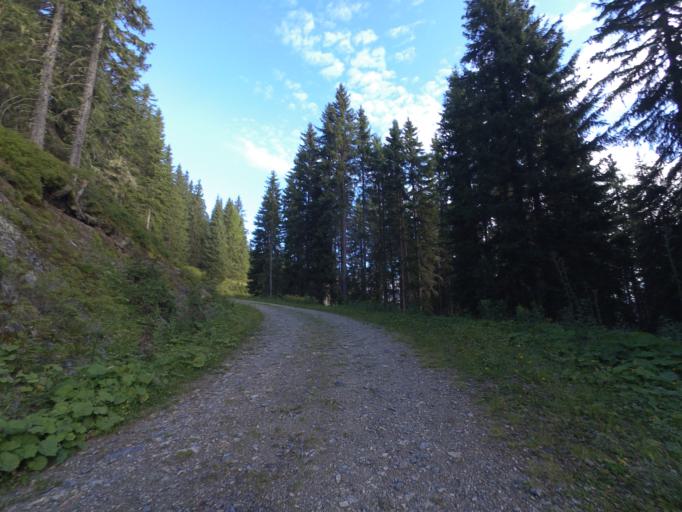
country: AT
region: Salzburg
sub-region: Politischer Bezirk Sankt Johann im Pongau
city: Goldegg
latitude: 47.3499
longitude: 13.0914
